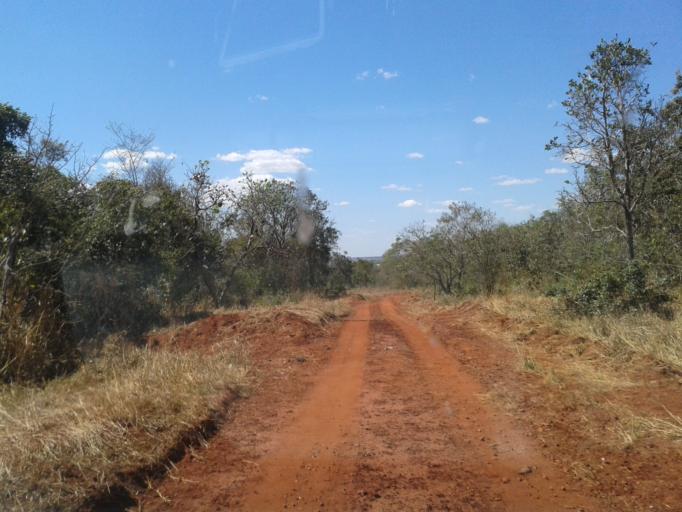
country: BR
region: Minas Gerais
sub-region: Santa Vitoria
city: Santa Vitoria
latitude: -19.0176
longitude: -50.4484
